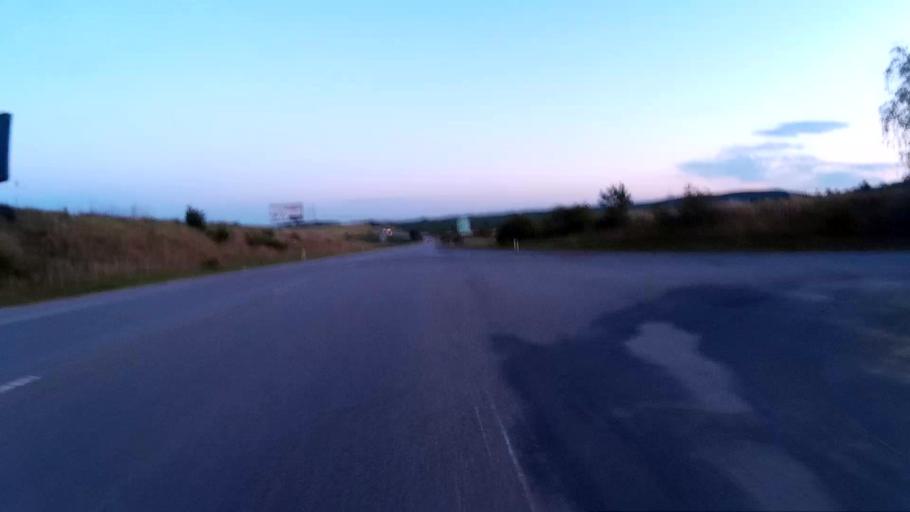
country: CZ
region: South Moravian
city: Troubsko
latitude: 49.1862
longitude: 16.5068
